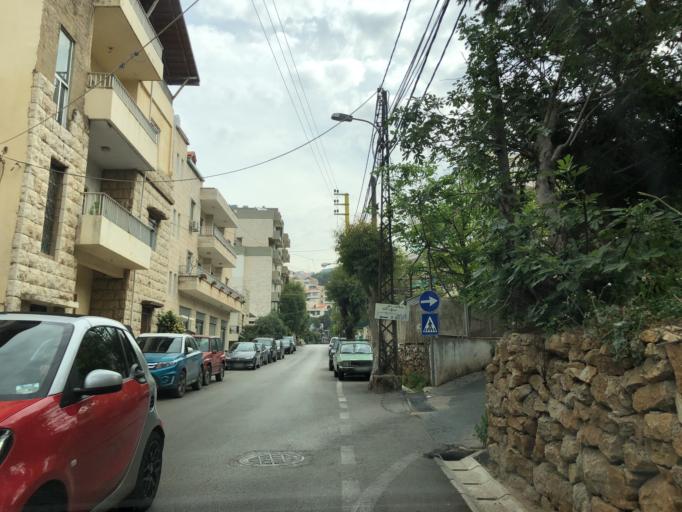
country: LB
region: Mont-Liban
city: Jdaidet el Matn
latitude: 33.8596
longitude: 35.5933
